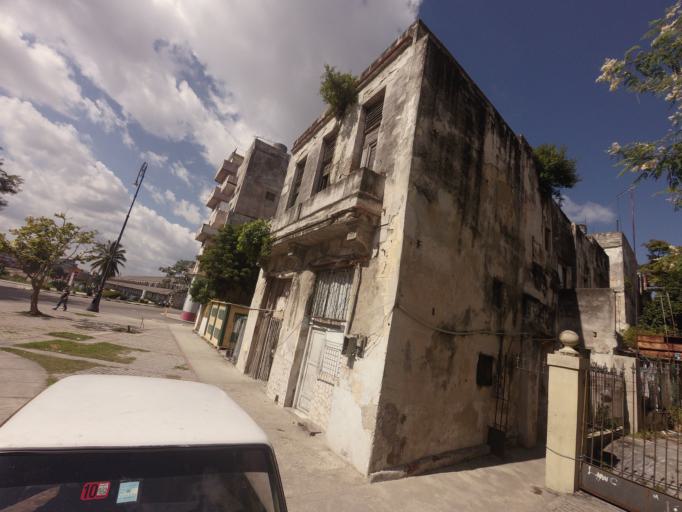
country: CU
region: La Habana
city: La Habana Vieja
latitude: 23.1288
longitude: -82.3525
